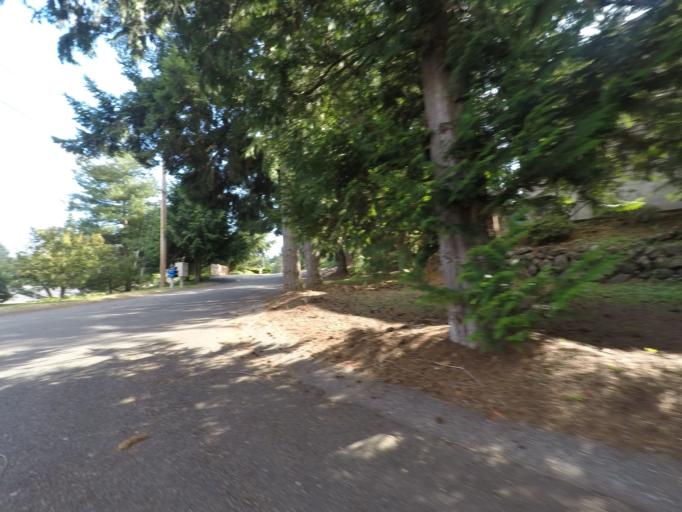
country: US
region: Washington
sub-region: Snohomish County
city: Brier
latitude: 47.7766
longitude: -122.2579
